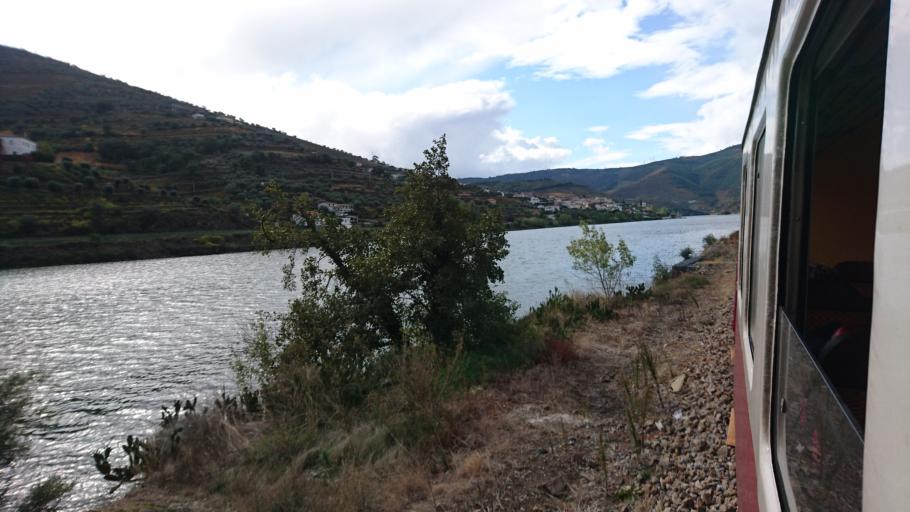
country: PT
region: Viseu
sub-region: Armamar
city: Armamar
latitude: 41.1593
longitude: -7.6732
